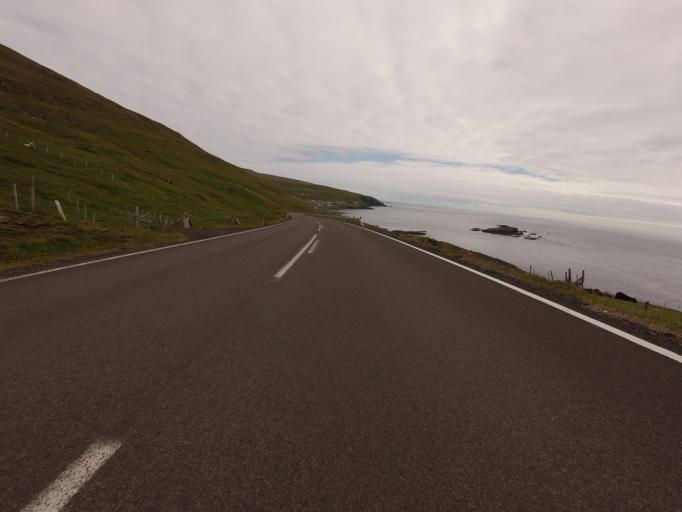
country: FO
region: Suduroy
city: Vagur
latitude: 61.4098
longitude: -6.7401
